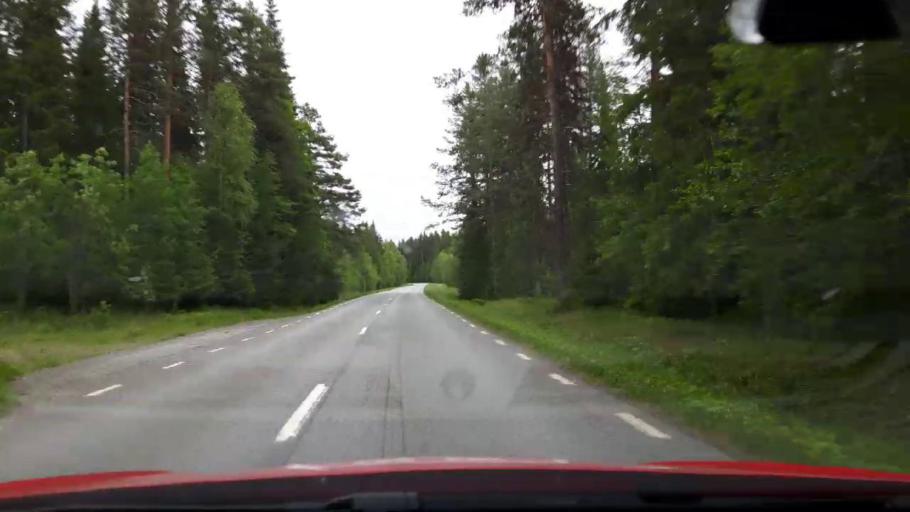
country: SE
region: Jaemtland
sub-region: Stroemsunds Kommun
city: Stroemsund
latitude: 63.4302
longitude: 15.5007
